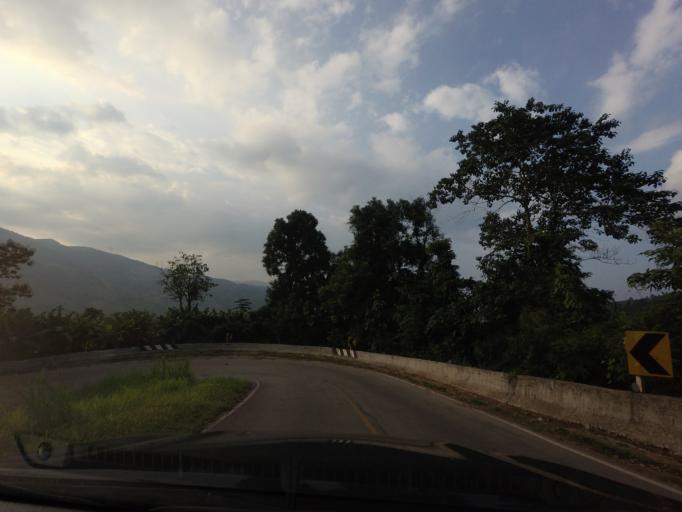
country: TH
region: Loei
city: Na Haeo
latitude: 17.3638
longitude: 101.0513
